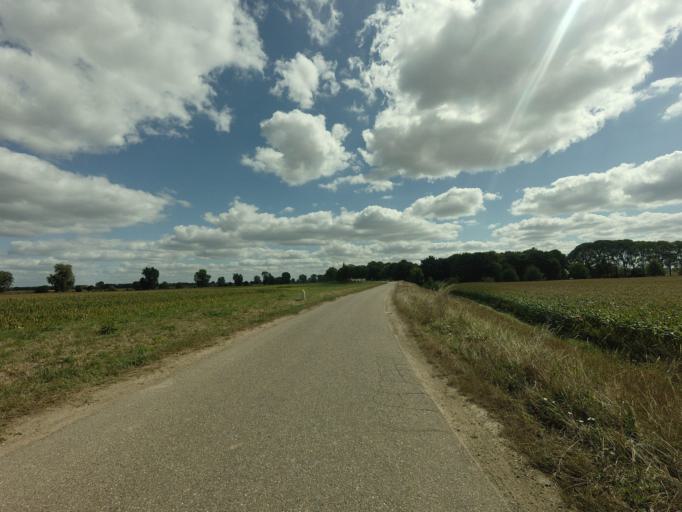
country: NL
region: North Brabant
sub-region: Gemeente Oss
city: Berghem
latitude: 51.8218
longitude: 5.6036
